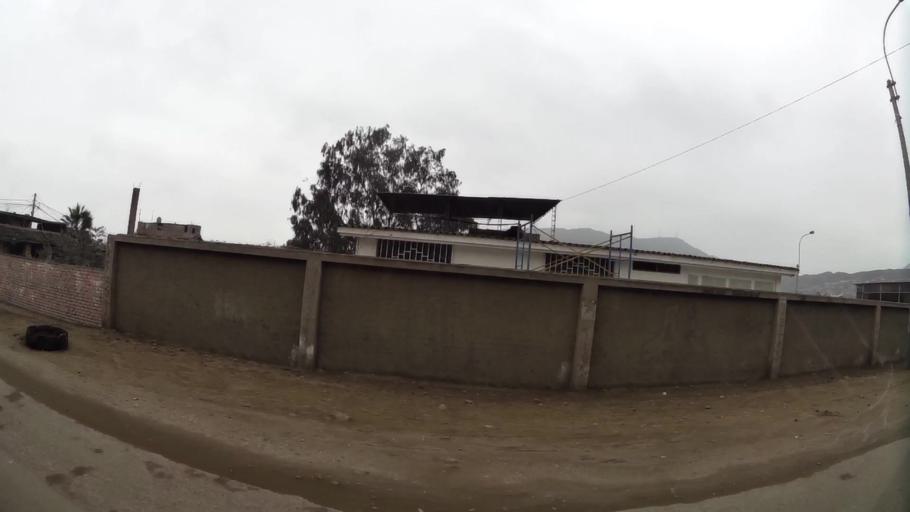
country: PE
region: Lima
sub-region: Lima
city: Cieneguilla
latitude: -12.2122
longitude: -76.9030
